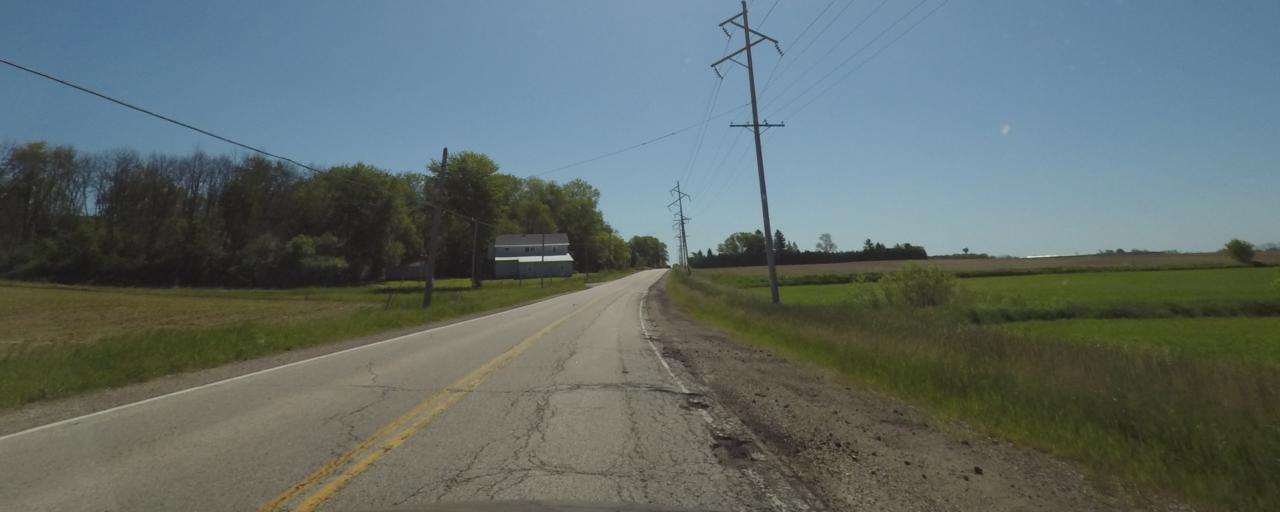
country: US
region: Wisconsin
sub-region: Sheboygan County
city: Sheboygan Falls
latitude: 43.7418
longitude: -87.8617
